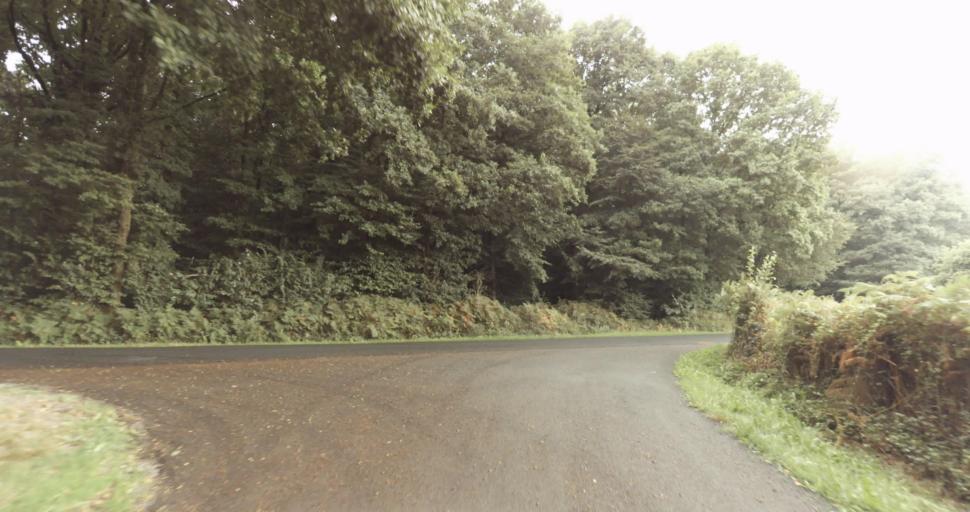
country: FR
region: Lower Normandy
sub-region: Departement de l'Orne
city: Vimoutiers
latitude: 48.8737
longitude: 0.1972
